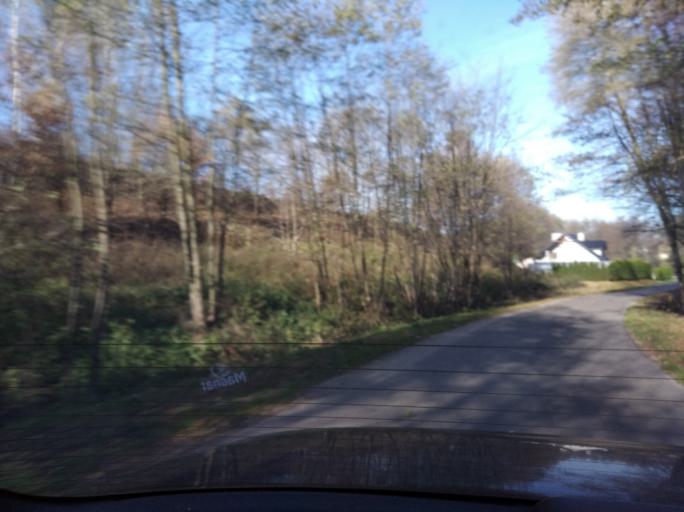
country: PL
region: Subcarpathian Voivodeship
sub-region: Powiat ropczycko-sedziszowski
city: Wielopole Skrzynskie
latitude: 49.9051
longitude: 21.5682
